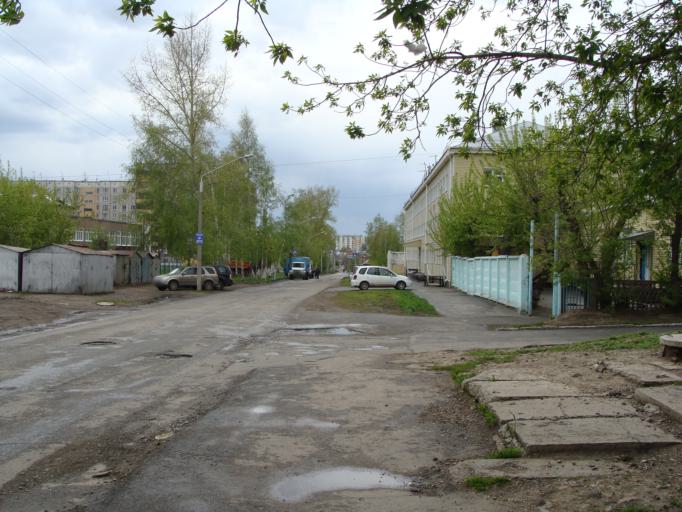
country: RU
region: Altai Krai
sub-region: Gorod Barnaulskiy
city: Barnaul
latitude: 53.3677
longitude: 83.7532
